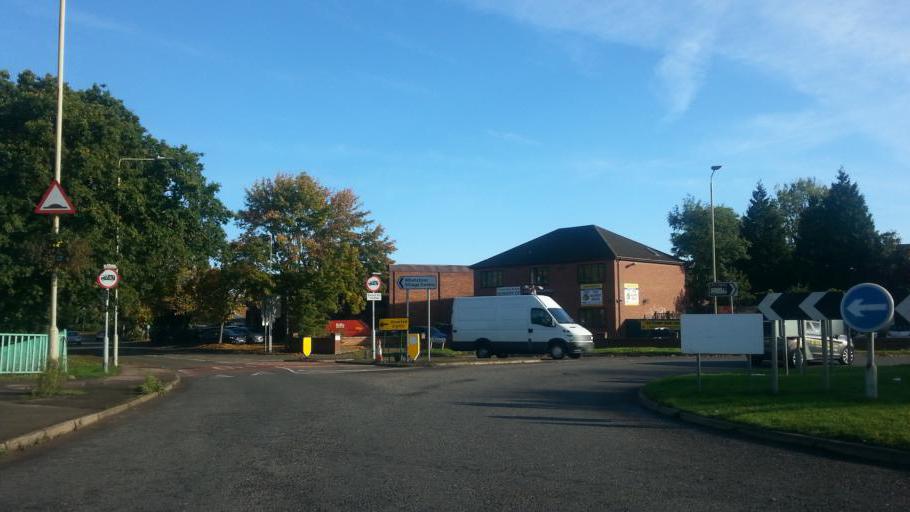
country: GB
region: England
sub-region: Leicestershire
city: Blaby
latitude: 52.5671
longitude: -1.1782
